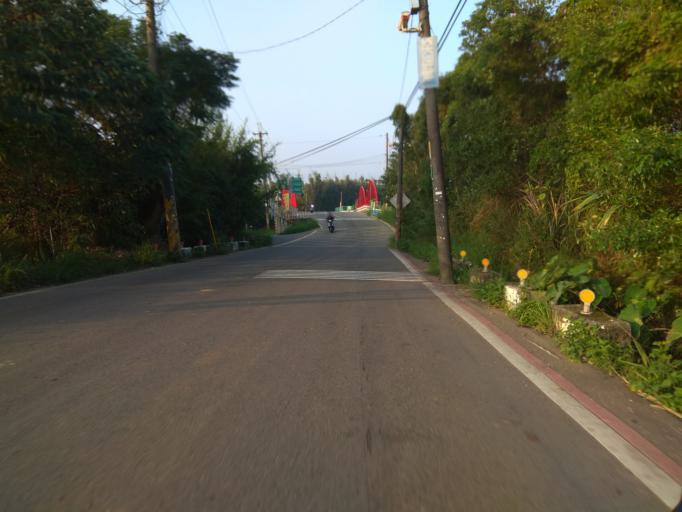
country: TW
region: Taiwan
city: Daxi
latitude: 24.9328
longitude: 121.2084
